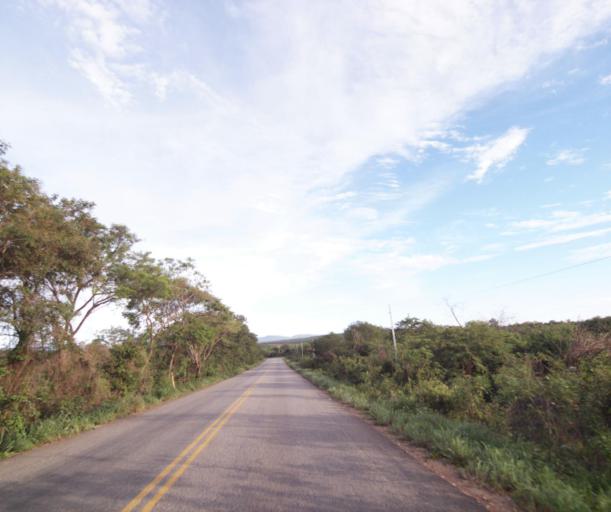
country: BR
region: Bahia
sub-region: Caetite
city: Caetite
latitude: -14.1690
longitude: -42.2985
